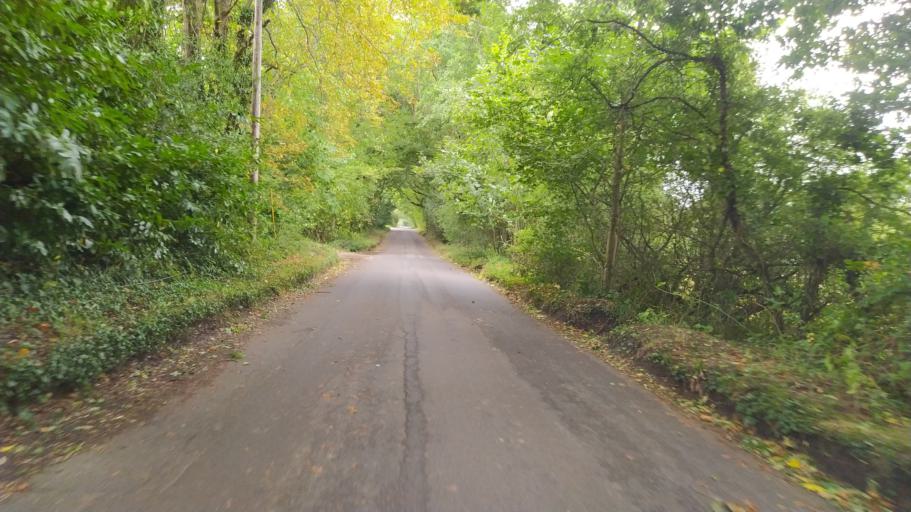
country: GB
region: England
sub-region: Dorset
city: Broadstone
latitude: 50.7653
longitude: -2.0297
